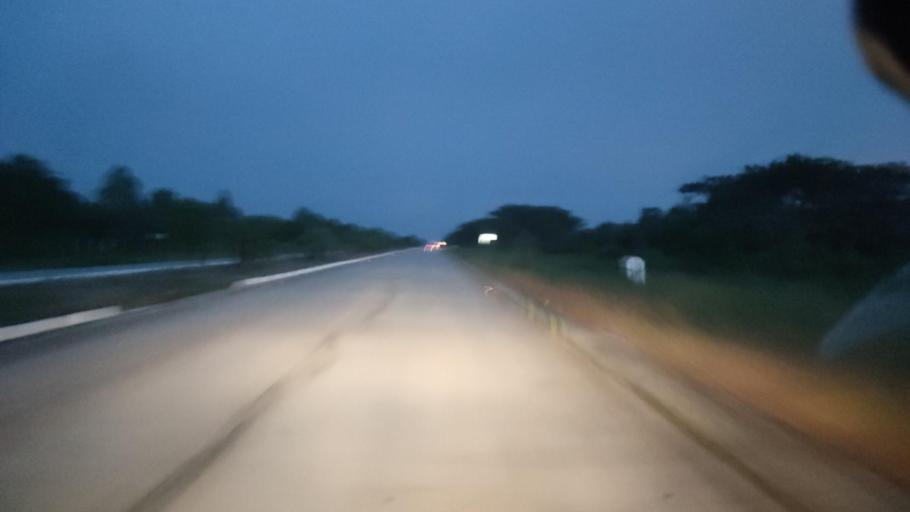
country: MM
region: Mandalay
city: Nay Pyi Taw
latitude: 19.9912
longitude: 95.9746
